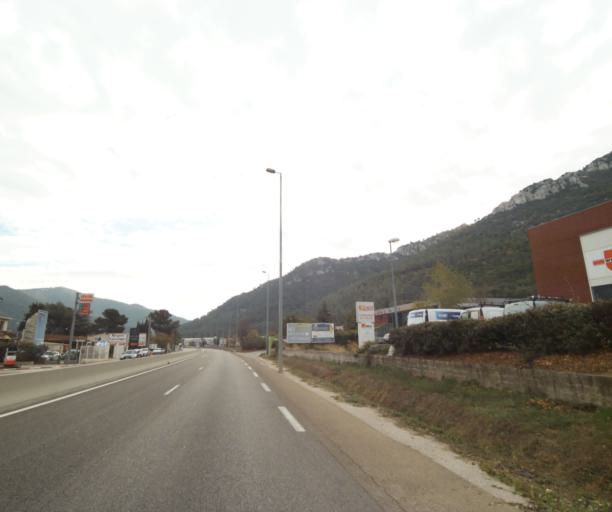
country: FR
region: Provence-Alpes-Cote d'Azur
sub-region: Departement des Bouches-du-Rhone
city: Gemenos
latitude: 43.2783
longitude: 5.6152
